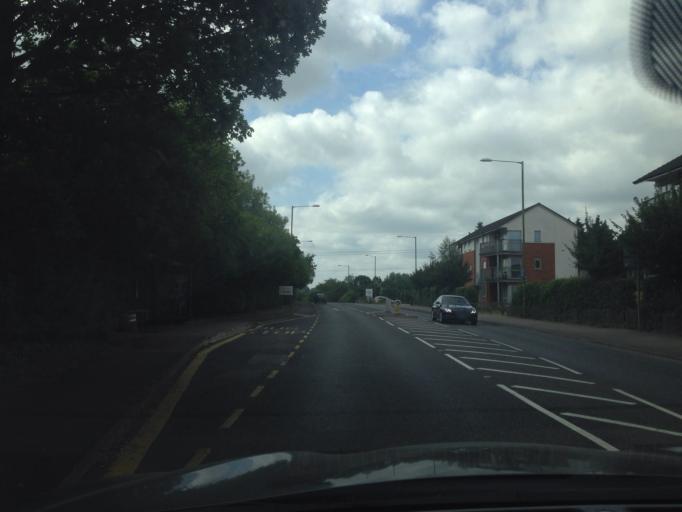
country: GB
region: England
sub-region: Hertfordshire
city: Bushey
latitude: 51.6646
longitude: -0.3634
